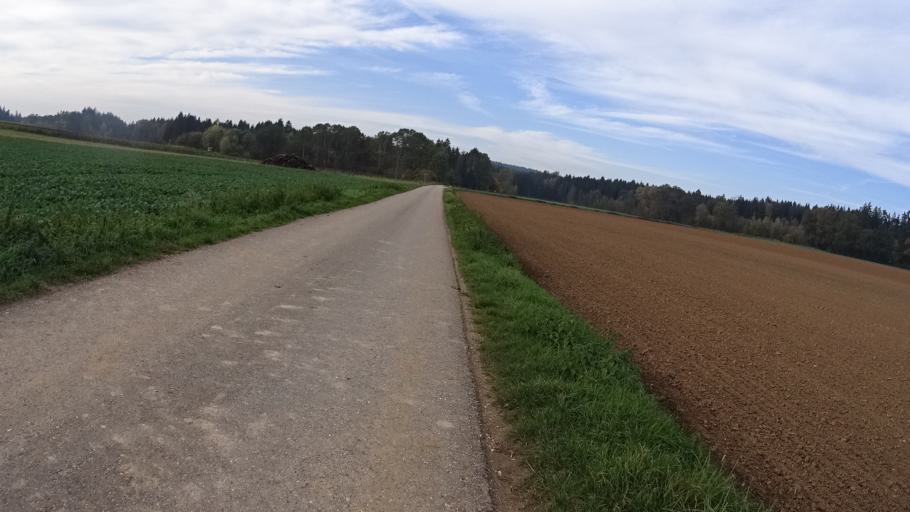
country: DE
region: Bavaria
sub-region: Upper Bavaria
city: Buxheim
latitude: 48.8310
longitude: 11.2705
